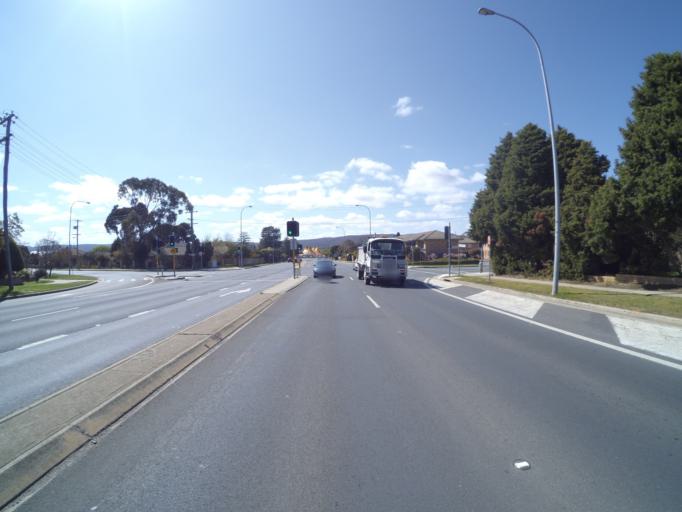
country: AU
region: New South Wales
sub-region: Queanbeyan
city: Queanbeyan
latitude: -35.3568
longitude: 149.2250
